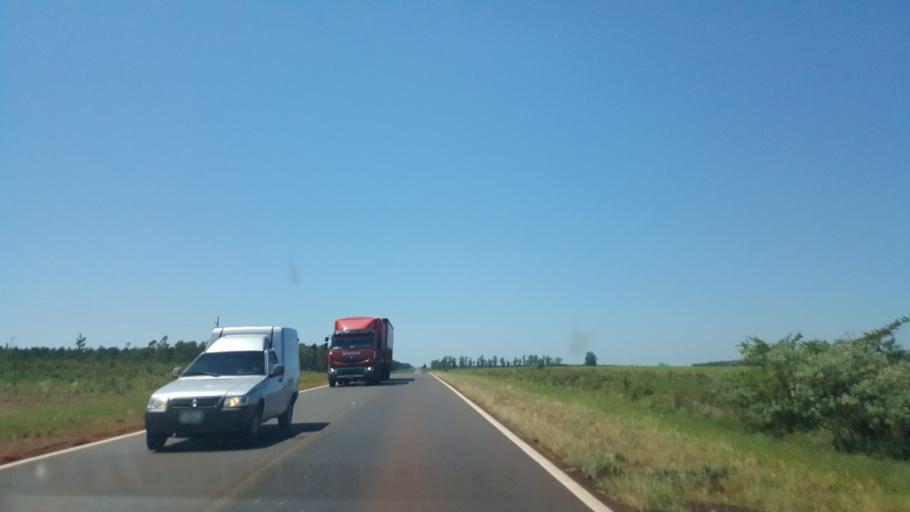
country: AR
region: Corrientes
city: Santo Tome
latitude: -28.4141
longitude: -56.1076
